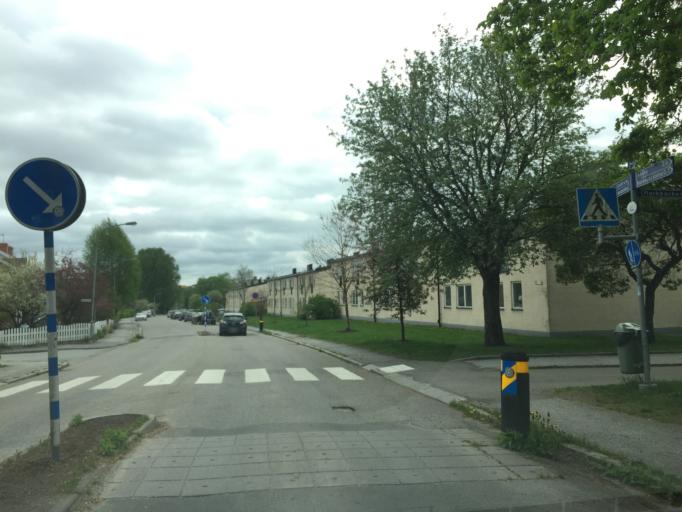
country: SE
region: OErebro
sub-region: Orebro Kommun
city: Orebro
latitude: 59.2824
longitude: 15.1932
